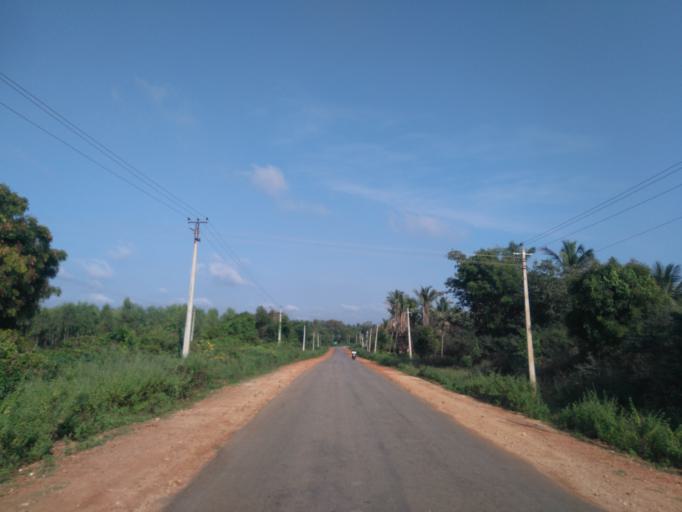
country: IN
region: Karnataka
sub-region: Chamrajnagar
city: Kollegal
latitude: 12.2599
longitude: 77.0455
